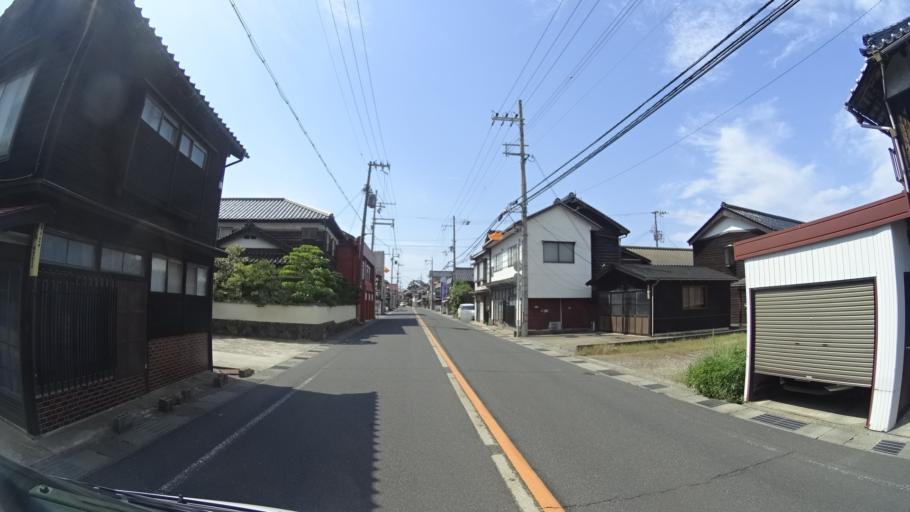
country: JP
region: Kyoto
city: Miyazu
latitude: 35.6859
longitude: 135.0236
